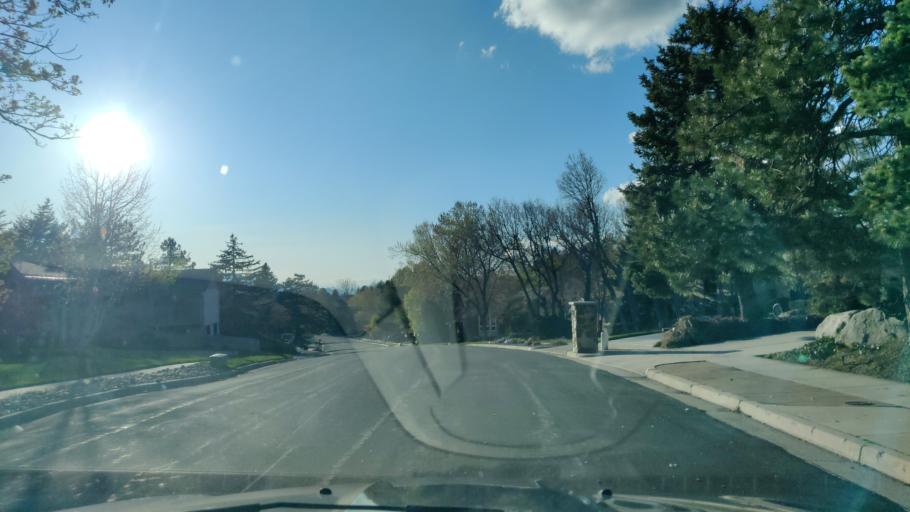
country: US
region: Utah
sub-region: Salt Lake County
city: Cottonwood Heights
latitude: 40.6139
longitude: -111.7924
